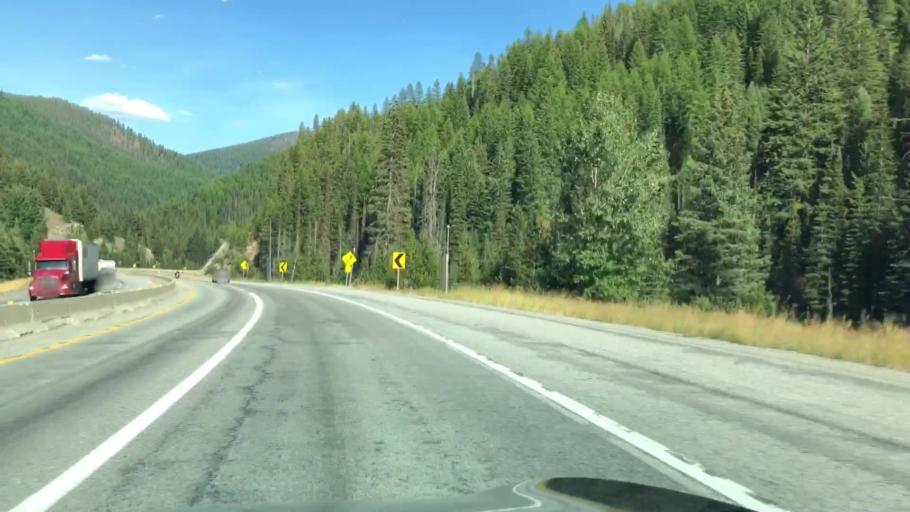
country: US
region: Idaho
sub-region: Shoshone County
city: Wallace
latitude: 47.4342
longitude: -115.6635
